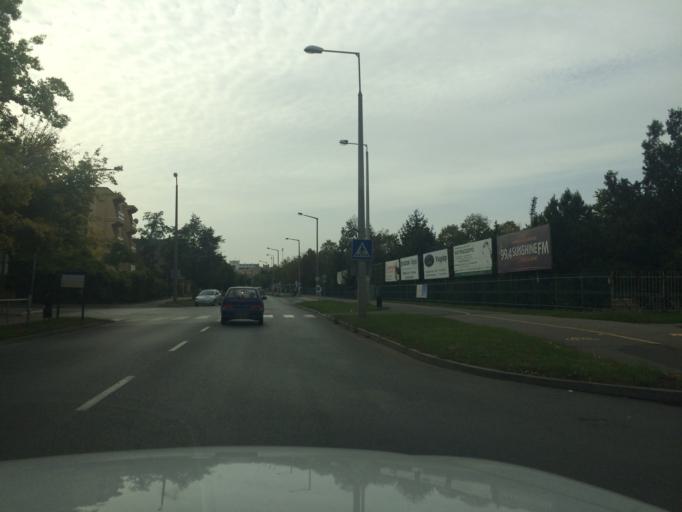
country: HU
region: Szabolcs-Szatmar-Bereg
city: Nyiregyhaza
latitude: 47.9717
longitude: 21.7159
